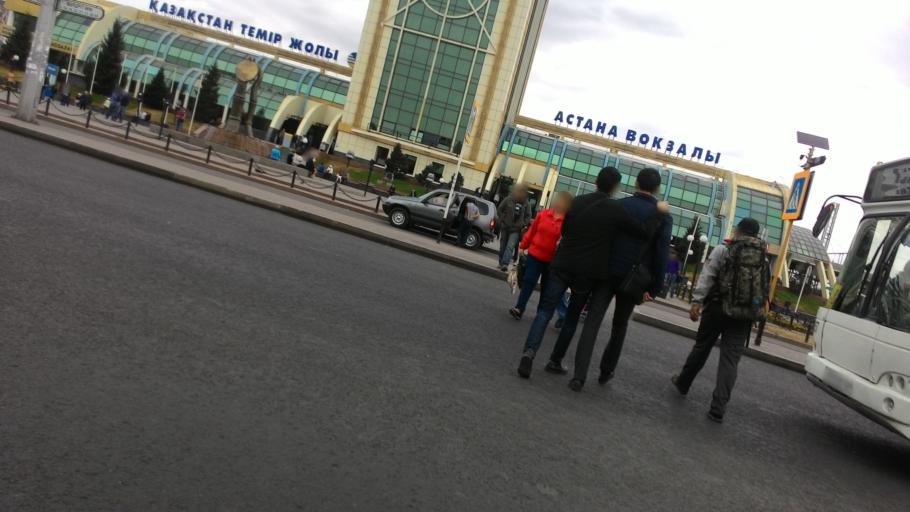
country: KZ
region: Astana Qalasy
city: Astana
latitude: 51.1945
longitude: 71.4092
